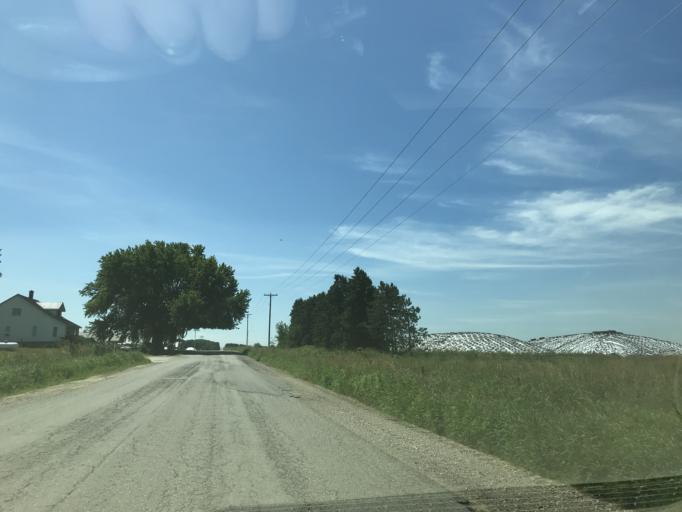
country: US
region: Michigan
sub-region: Missaukee County
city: Lake City
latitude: 44.3138
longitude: -85.0748
